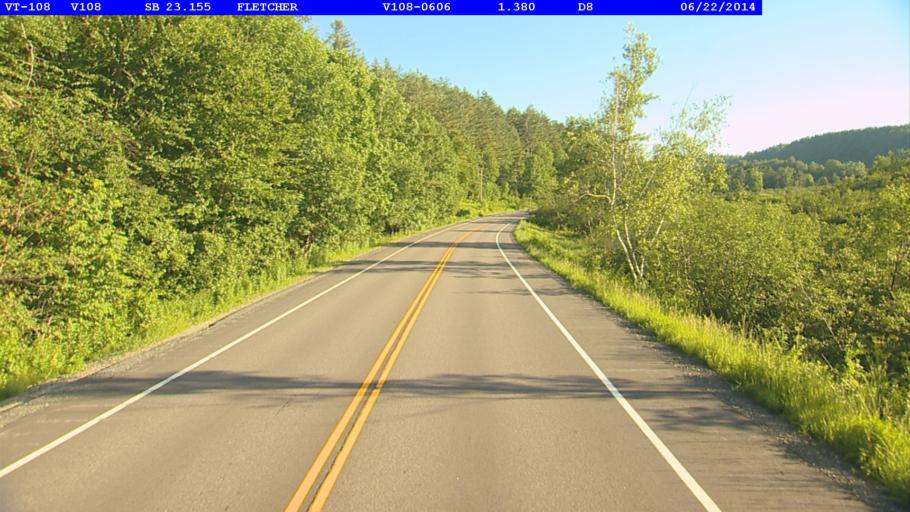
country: US
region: Vermont
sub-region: Lamoille County
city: Johnson
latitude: 44.7201
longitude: -72.8311
